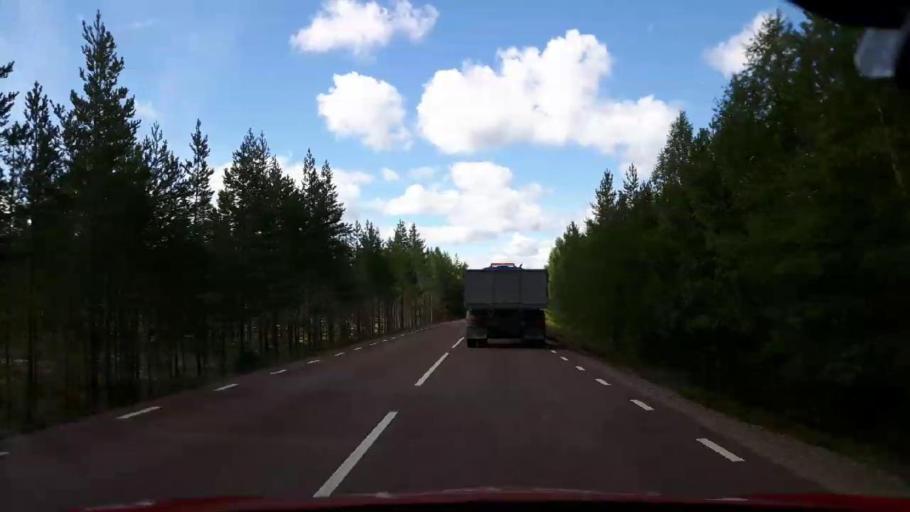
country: SE
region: Jaemtland
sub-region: Harjedalens Kommun
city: Sveg
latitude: 62.0055
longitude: 14.2975
